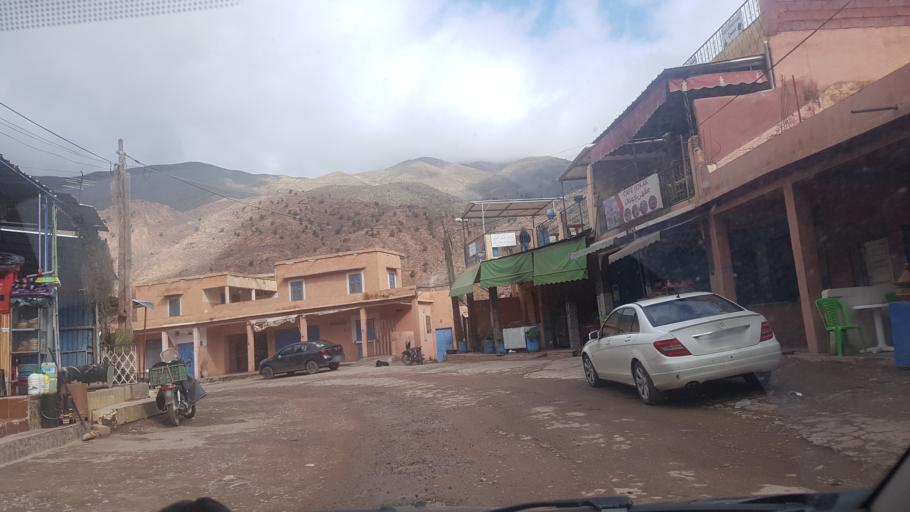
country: MA
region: Marrakech-Tensift-Al Haouz
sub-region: Al-Haouz
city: Azgour
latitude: 30.9997
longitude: -8.1582
